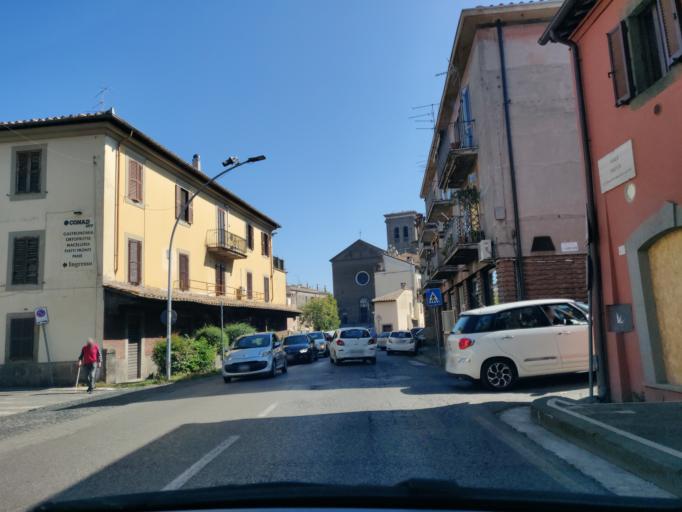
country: IT
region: Latium
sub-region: Provincia di Viterbo
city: Viterbo
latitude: 42.4291
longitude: 12.1271
